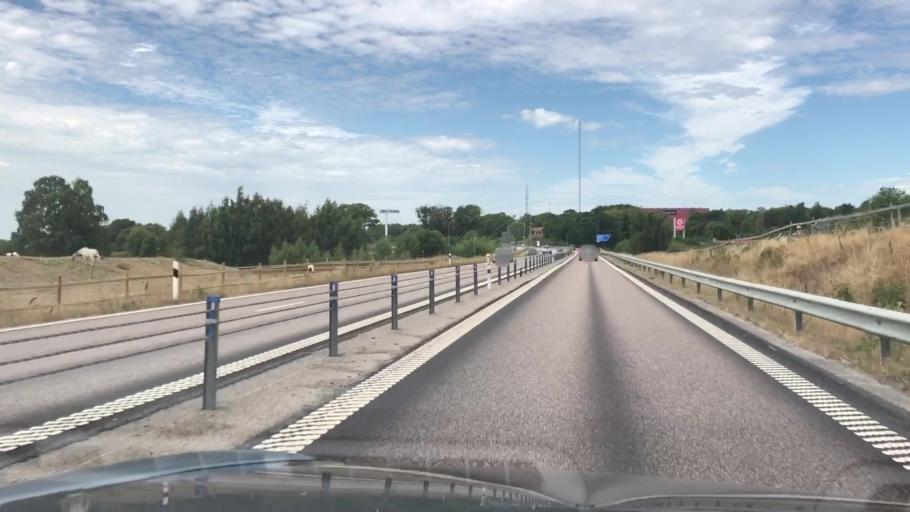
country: SE
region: Blekinge
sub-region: Karlskrona Kommun
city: Rodeby
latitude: 56.2051
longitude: 15.6476
